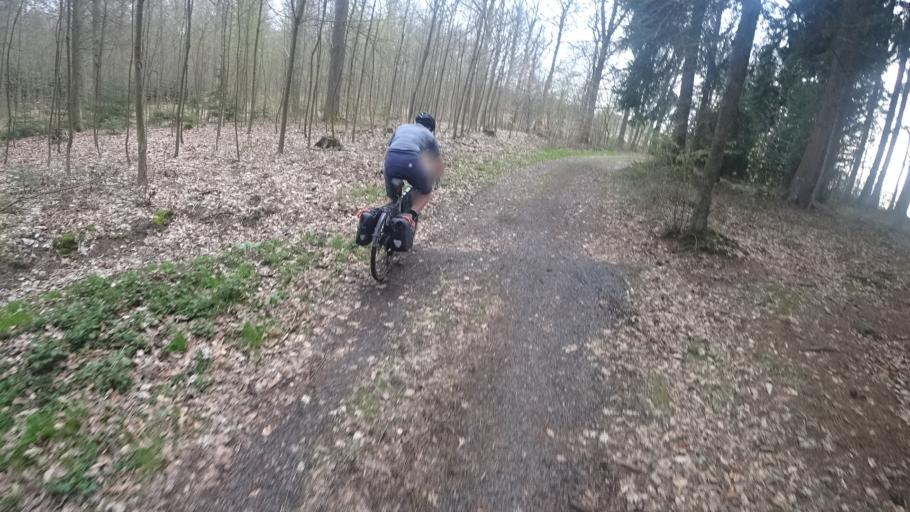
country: DE
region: Rheinland-Pfalz
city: Dickendorf
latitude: 50.7300
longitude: 7.8307
